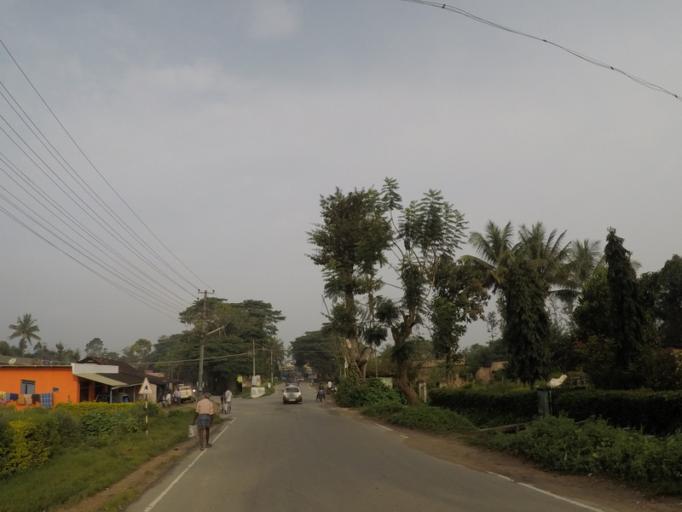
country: IN
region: Karnataka
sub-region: Chikmagalur
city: Mudigere
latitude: 13.2450
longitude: 75.6455
